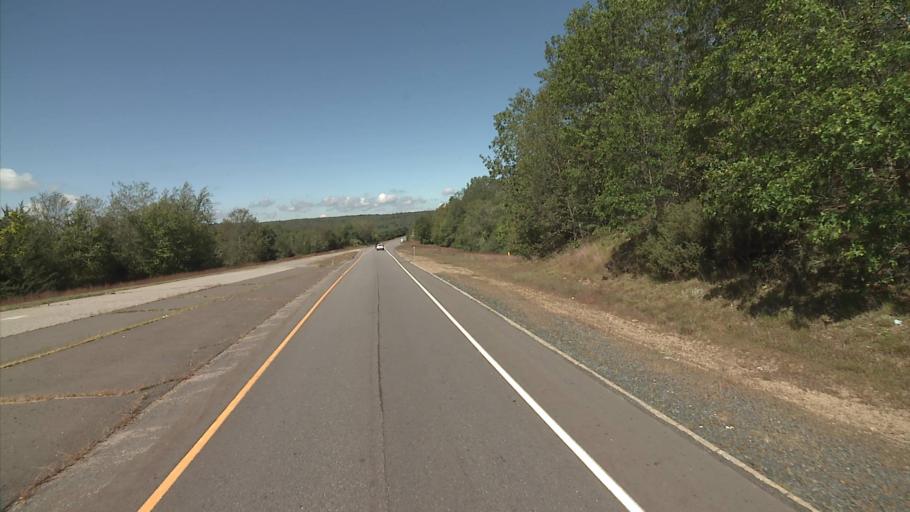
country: US
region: Connecticut
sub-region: New London County
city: Colchester
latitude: 41.4668
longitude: -72.2805
